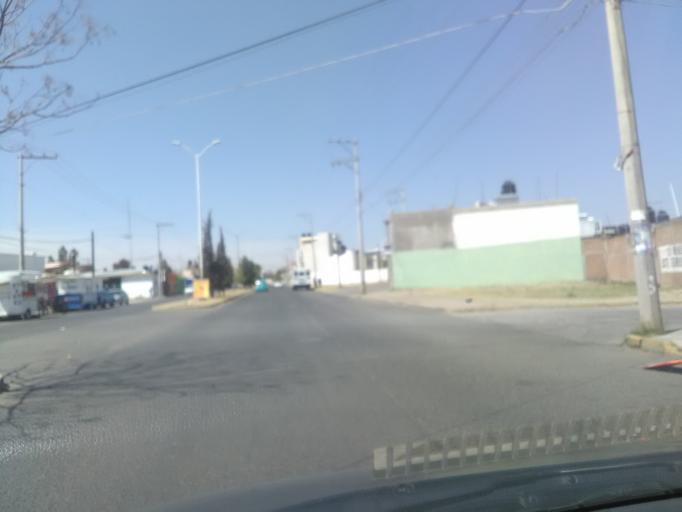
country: MX
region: Durango
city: Victoria de Durango
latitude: 24.0389
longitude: -104.6499
